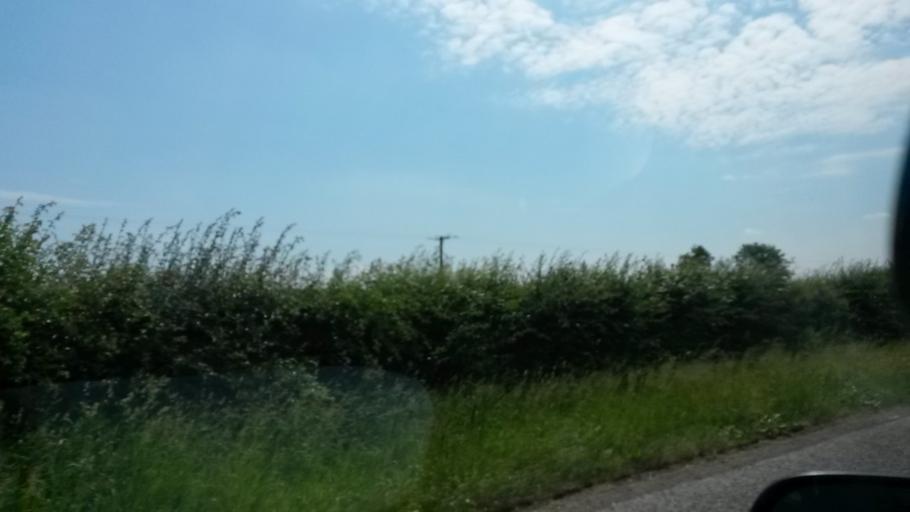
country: IE
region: Leinster
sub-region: An Mhi
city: Slane
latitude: 53.7037
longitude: -6.5798
